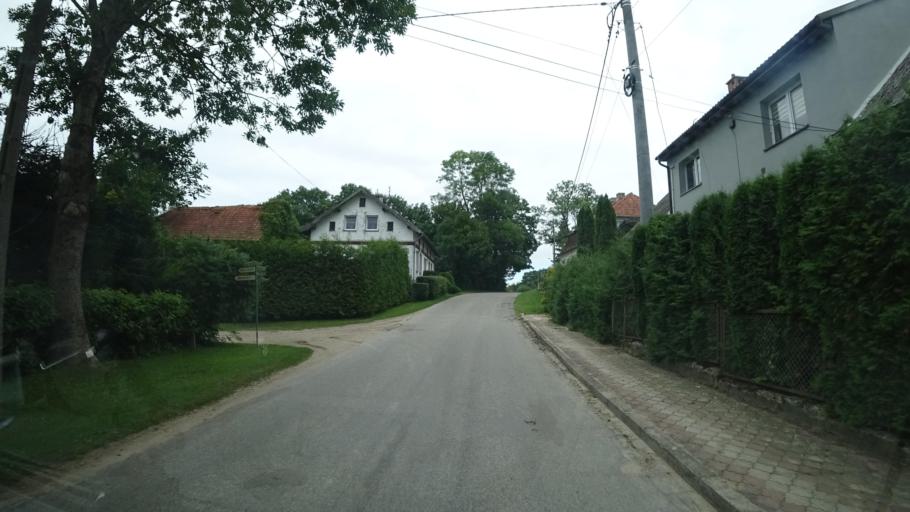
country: PL
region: Podlasie
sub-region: Powiat suwalski
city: Filipow
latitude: 54.2882
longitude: 22.5635
